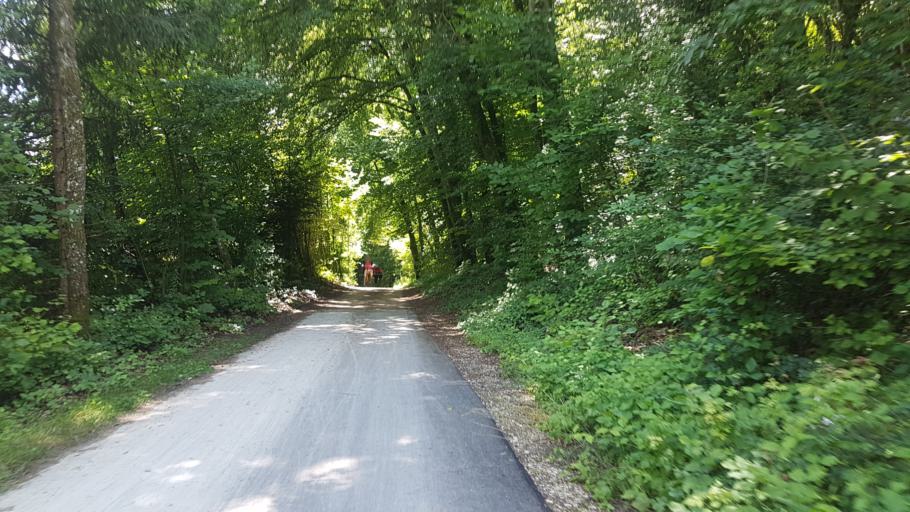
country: DE
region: Bavaria
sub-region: Regierungsbezirk Mittelfranken
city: Solnhofen
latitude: 48.8852
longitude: 11.0408
